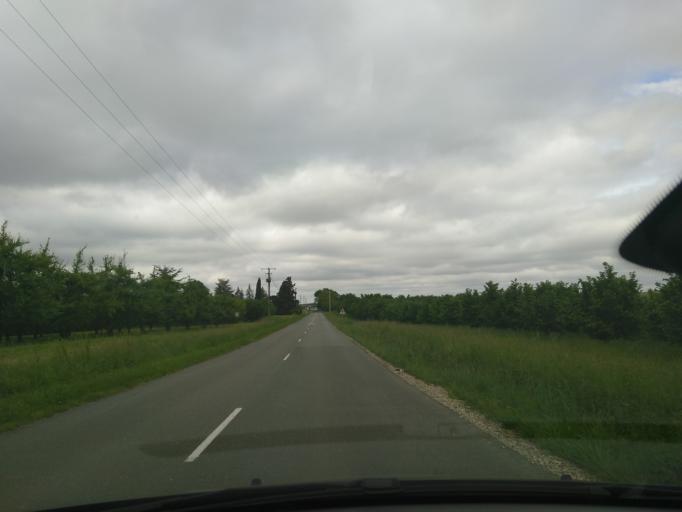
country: FR
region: Aquitaine
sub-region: Departement du Lot-et-Garonne
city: Cancon
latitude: 44.5402
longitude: 0.6074
